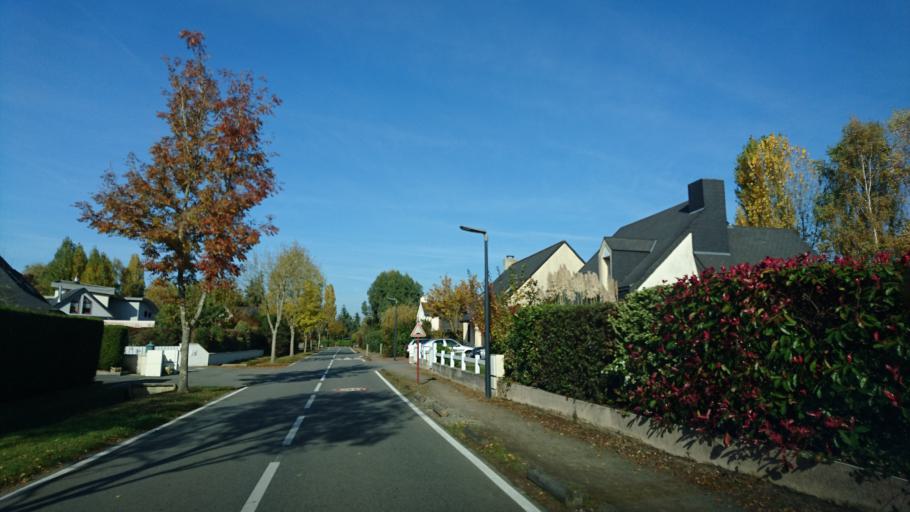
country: FR
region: Brittany
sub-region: Departement d'Ille-et-Vilaine
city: Bruz
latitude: 48.0343
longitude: -1.7680
